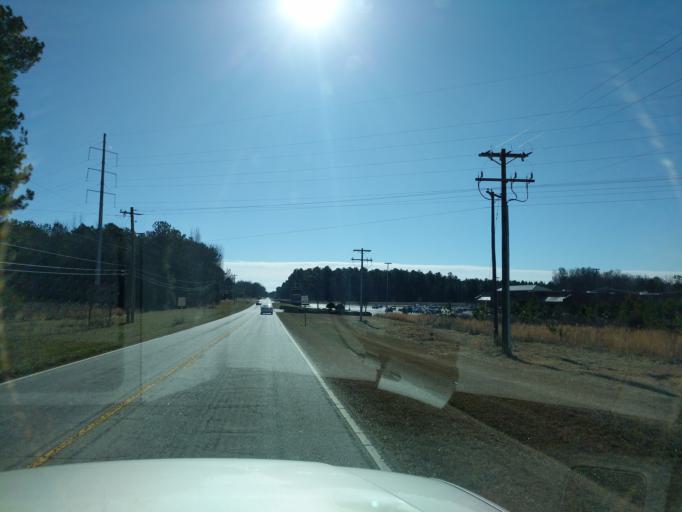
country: US
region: South Carolina
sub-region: Laurens County
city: Clinton
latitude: 34.4502
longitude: -81.8743
